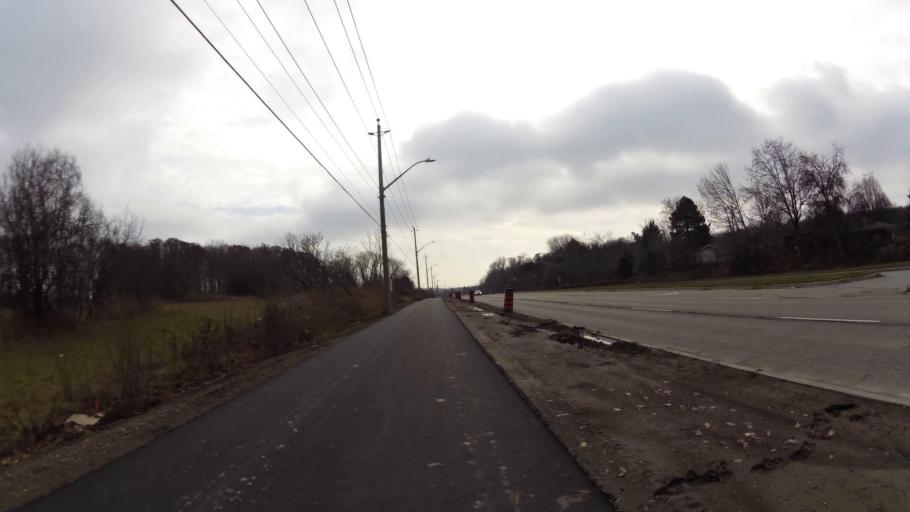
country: CA
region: Ontario
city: Kitchener
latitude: 43.4127
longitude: -80.4639
